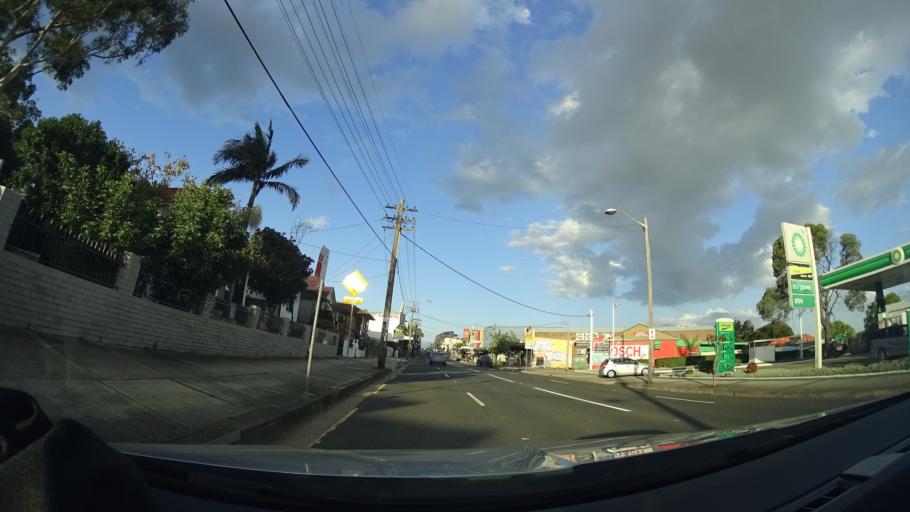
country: AU
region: New South Wales
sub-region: Ashfield
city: Croydon
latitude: -33.8961
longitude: 151.1050
